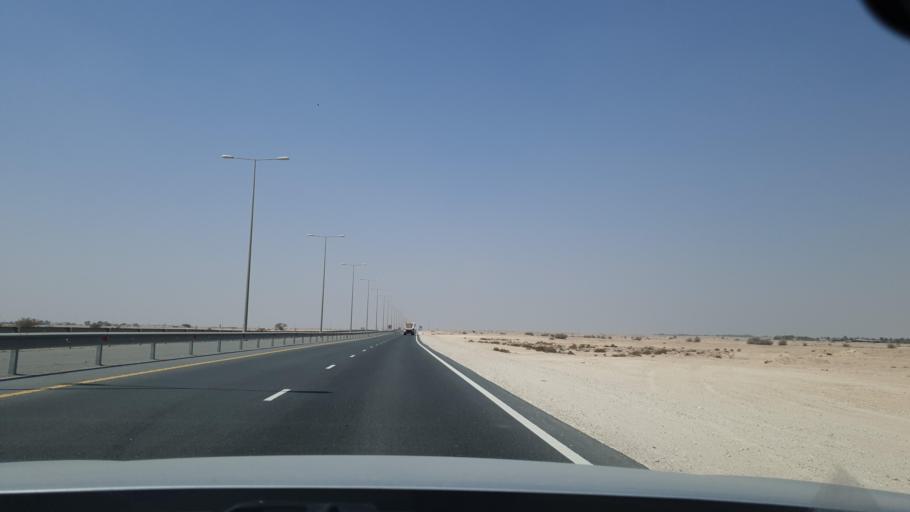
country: QA
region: Baladiyat az Za`ayin
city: Az Za`ayin
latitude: 25.6205
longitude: 51.3499
